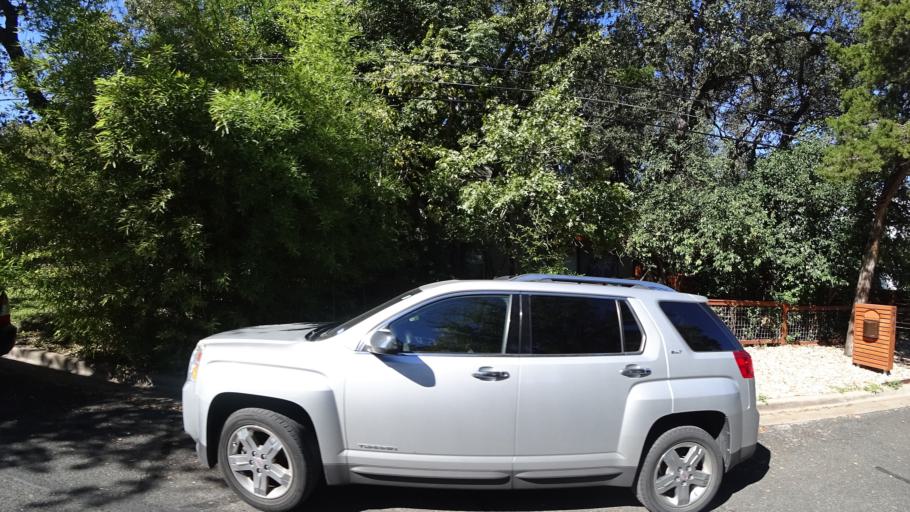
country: US
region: Texas
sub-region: Travis County
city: Austin
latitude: 30.2389
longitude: -97.7657
